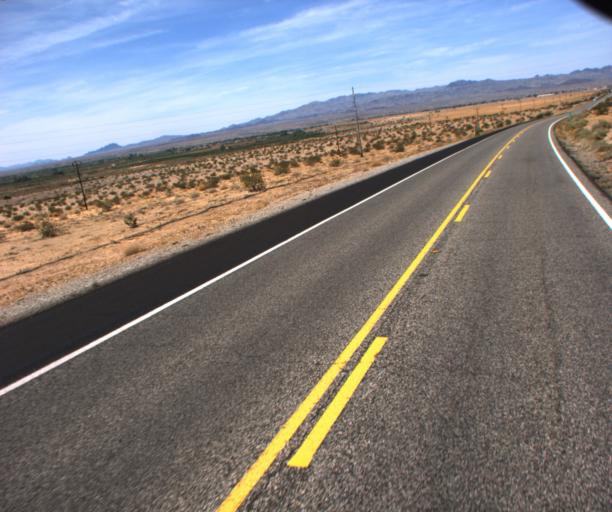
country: US
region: Arizona
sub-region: La Paz County
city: Parker
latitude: 34.0942
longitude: -114.2766
